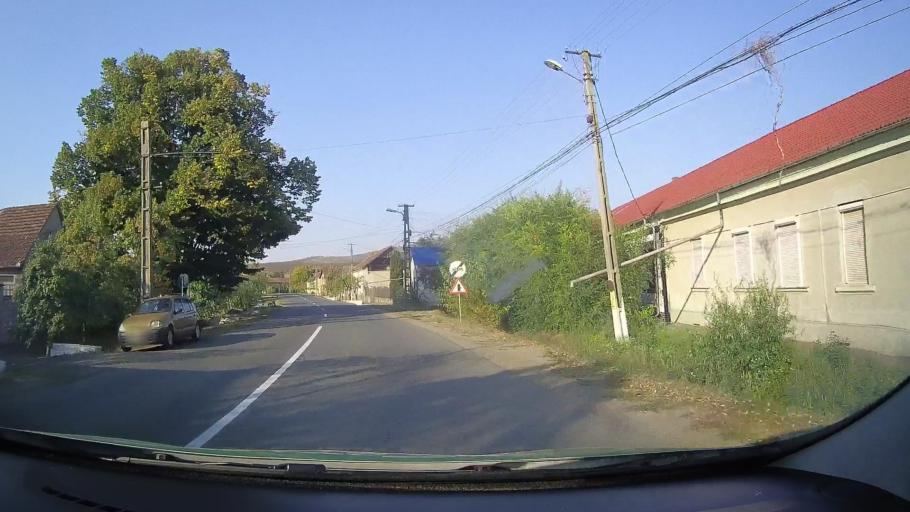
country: RO
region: Arad
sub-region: Comuna Ghioroc
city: Ghioroc
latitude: 46.1364
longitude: 21.6047
